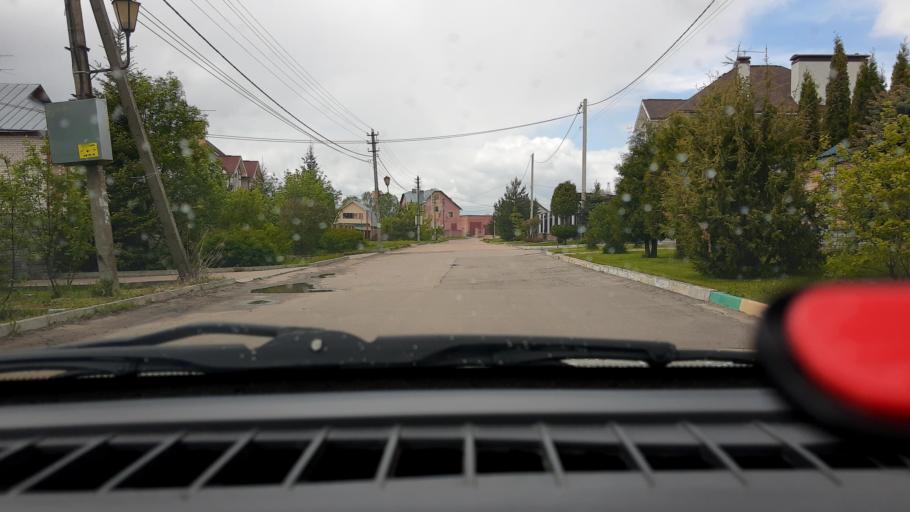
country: RU
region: Nizjnij Novgorod
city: Afonino
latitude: 56.2062
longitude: 43.9925
